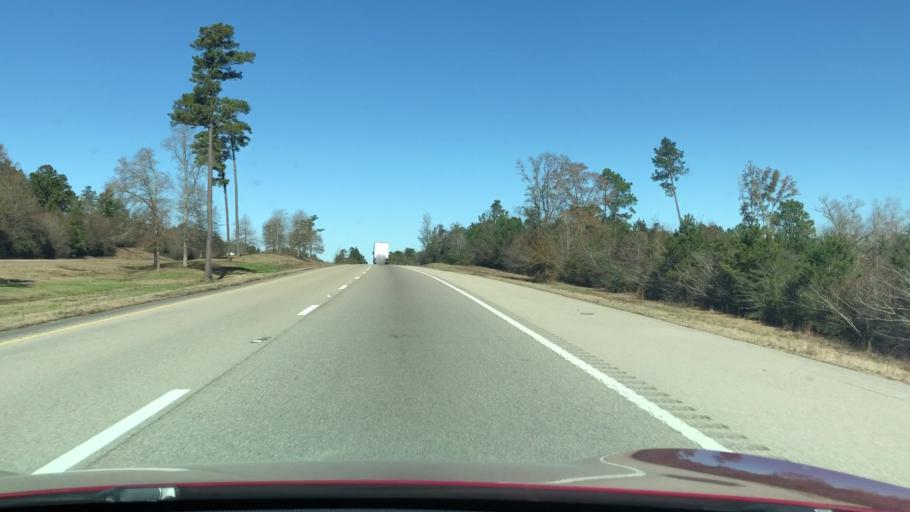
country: US
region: Mississippi
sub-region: Pearl River County
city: Poplarville
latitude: 30.7563
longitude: -89.5215
